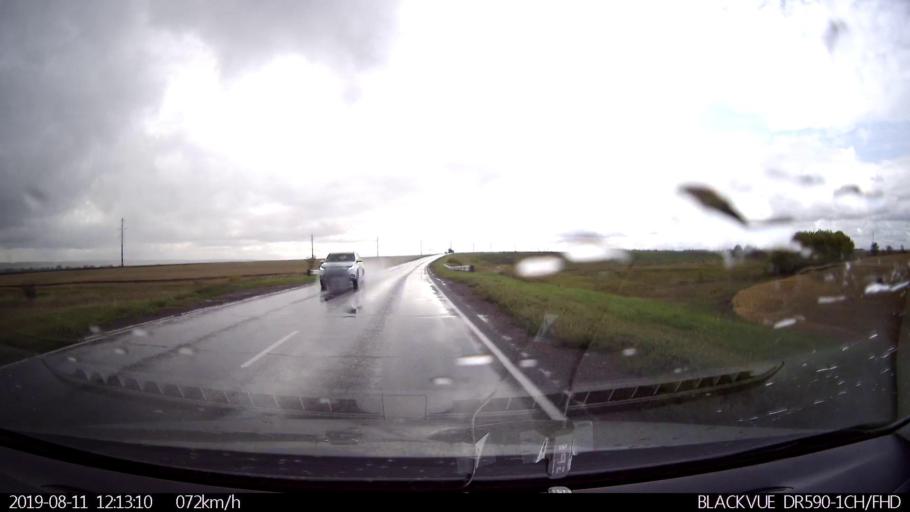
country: RU
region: Ulyanovsk
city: Silikatnyy
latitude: 53.9646
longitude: 47.9936
